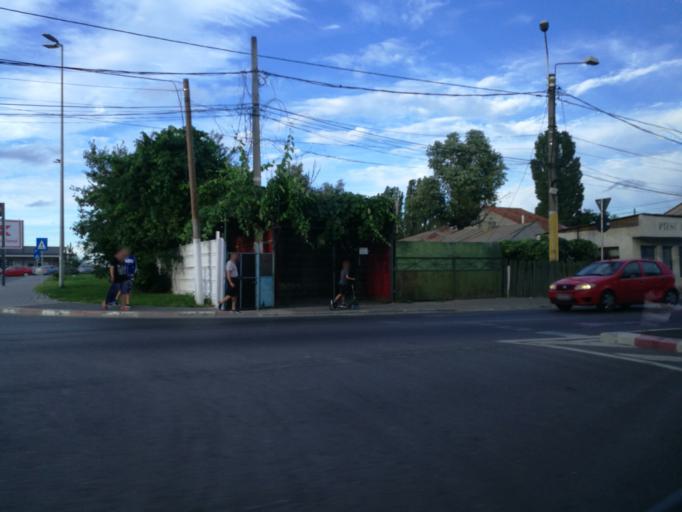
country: RO
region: Constanta
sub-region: Municipiul Constanta
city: Constanta
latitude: 44.1530
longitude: 28.6205
